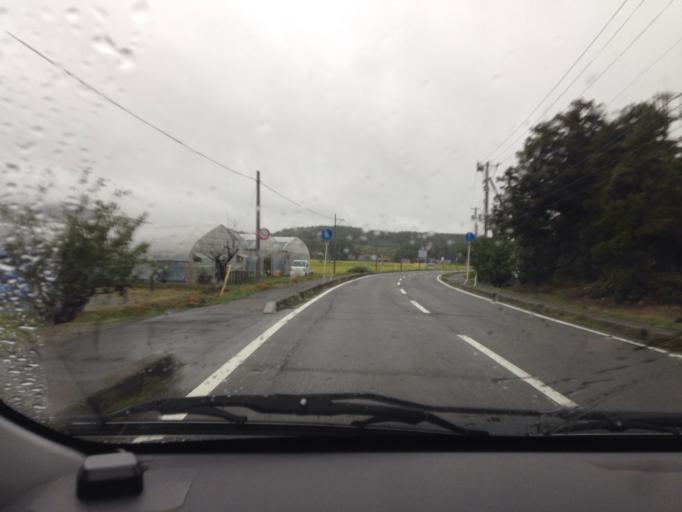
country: JP
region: Fukushima
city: Koriyama
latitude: 37.3991
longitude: 140.2683
